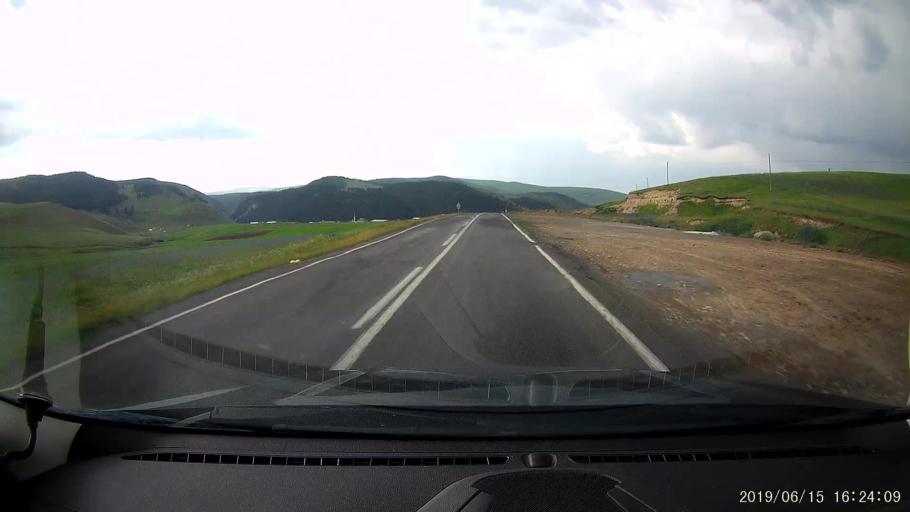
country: TR
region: Ardahan
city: Hanak
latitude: 41.1683
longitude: 42.8686
